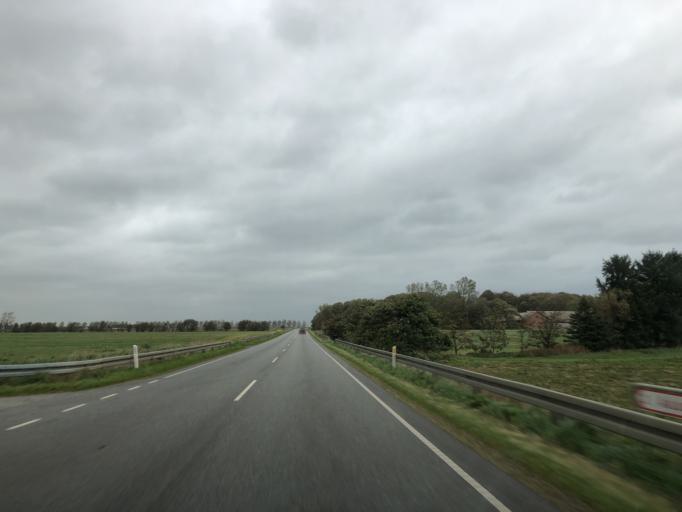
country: DK
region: Central Jutland
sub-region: Herning Kommune
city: Avlum
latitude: 56.2490
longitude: 8.7766
